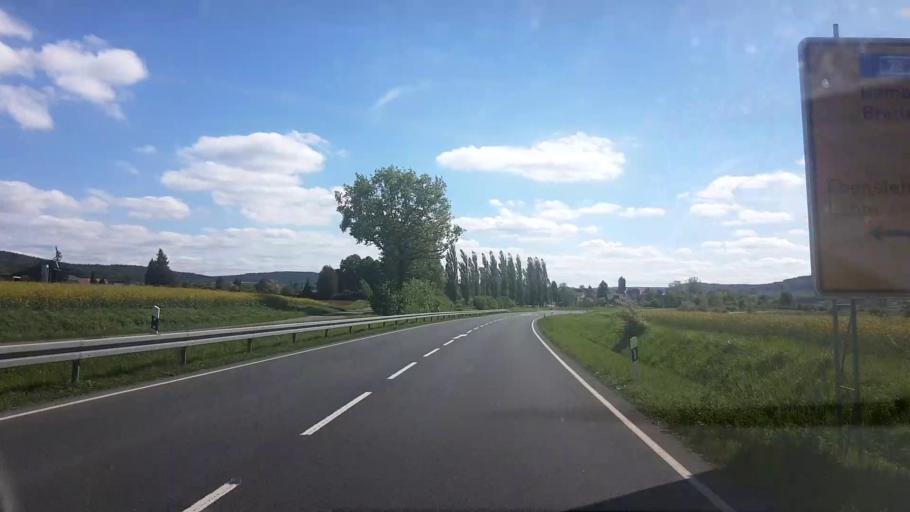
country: DE
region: Bavaria
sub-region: Regierungsbezirk Unterfranken
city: Untermerzbach
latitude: 50.1084
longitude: 10.8693
